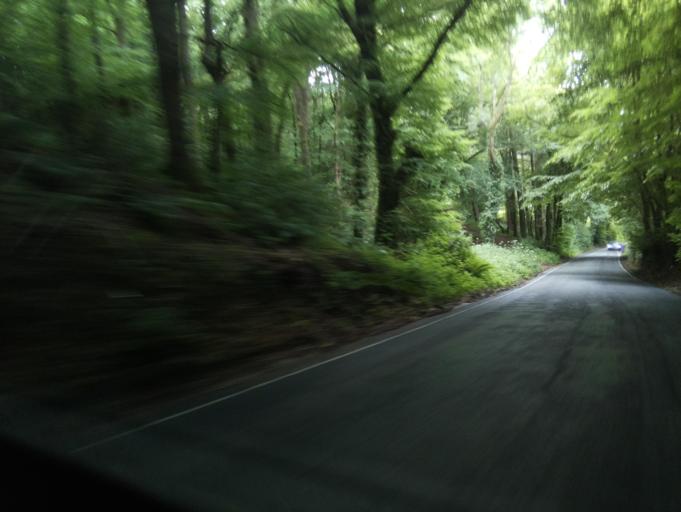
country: GB
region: England
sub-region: Devon
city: Ottery St Mary
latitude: 50.7545
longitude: -3.2369
